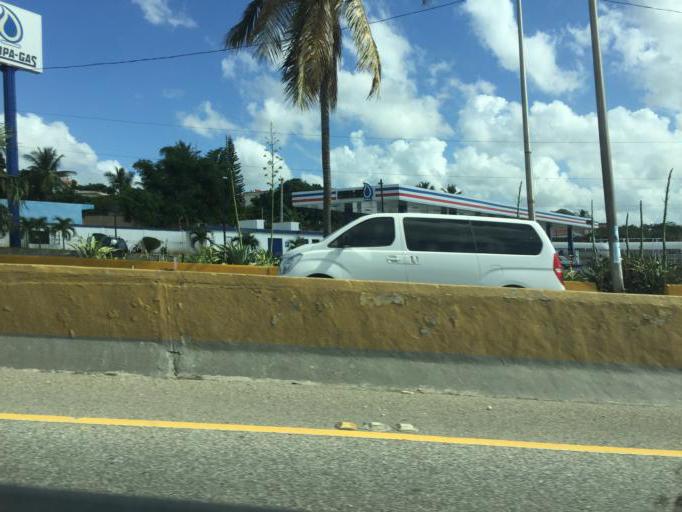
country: DO
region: Santo Domingo
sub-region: Santo Domingo
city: Santo Domingo Este
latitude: 18.4765
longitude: -69.8355
